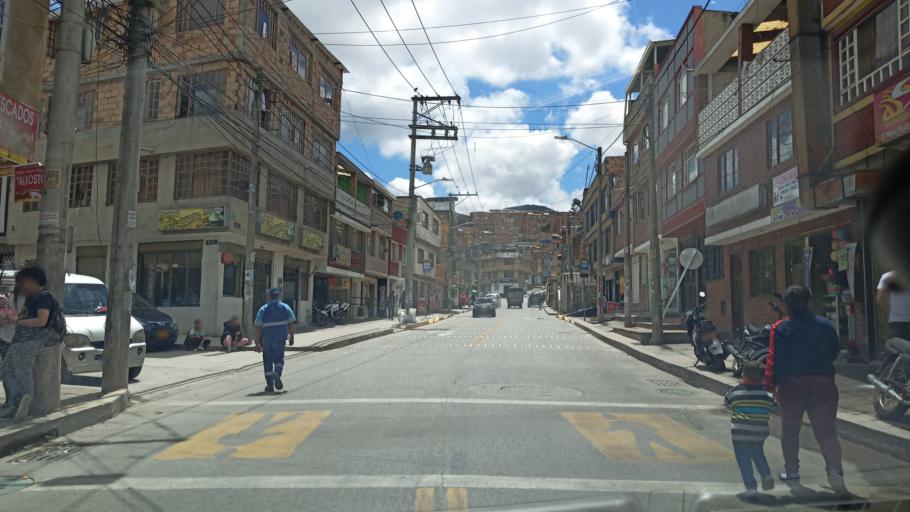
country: CO
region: Bogota D.C.
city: Bogota
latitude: 4.5668
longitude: -74.1141
